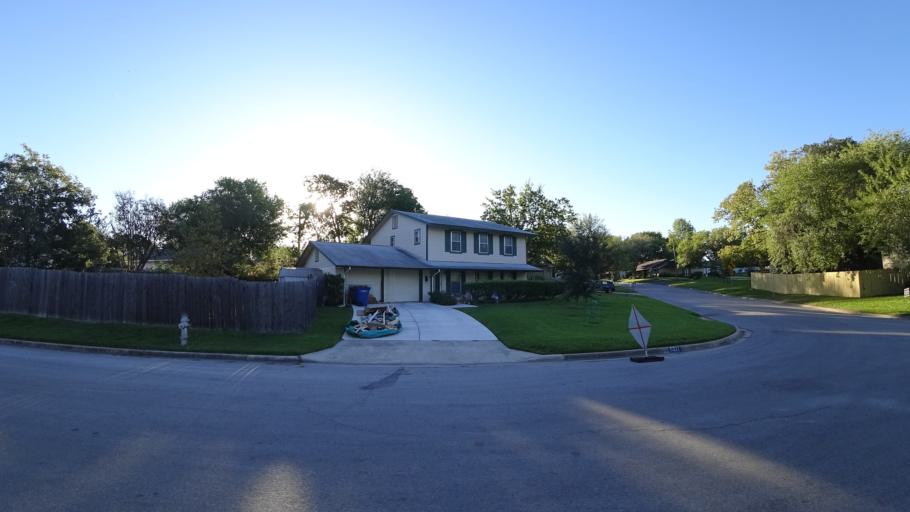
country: US
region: Texas
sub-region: Travis County
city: Austin
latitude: 30.2997
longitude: -97.6760
